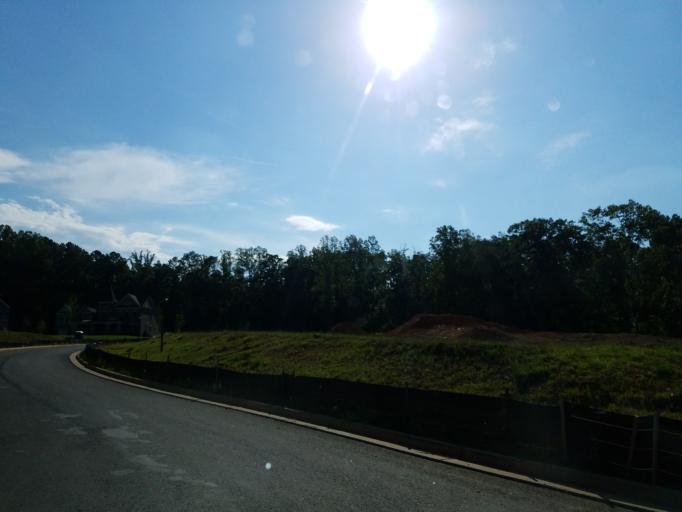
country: US
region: Georgia
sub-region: Fulton County
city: Milton
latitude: 34.1587
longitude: -84.3405
